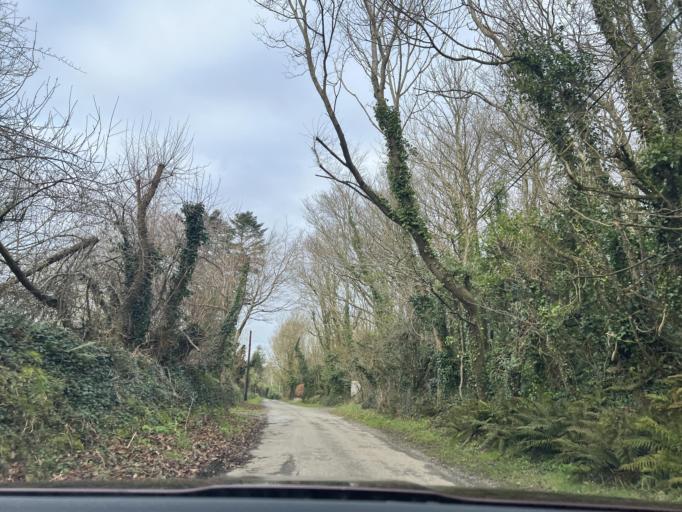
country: IE
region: Leinster
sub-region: Loch Garman
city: Loch Garman
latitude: 52.3709
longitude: -6.5355
